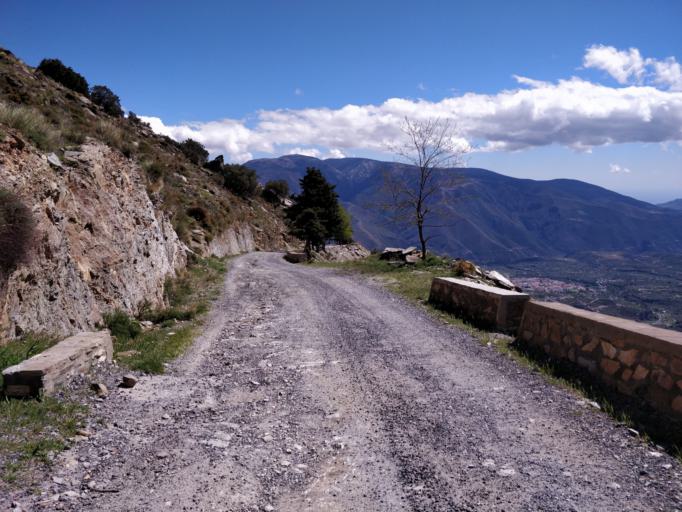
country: ES
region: Andalusia
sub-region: Provincia de Granada
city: Soportujar
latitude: 36.9372
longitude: -3.4035
